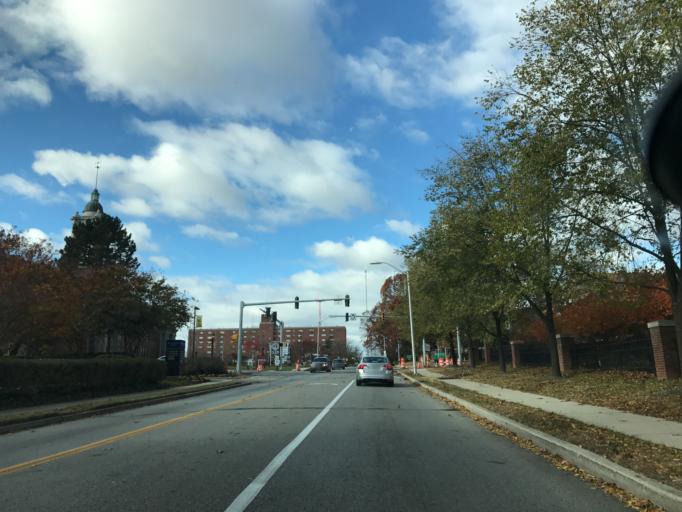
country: US
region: Maryland
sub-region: City of Baltimore
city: Baltimore
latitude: 39.3372
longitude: -76.6290
